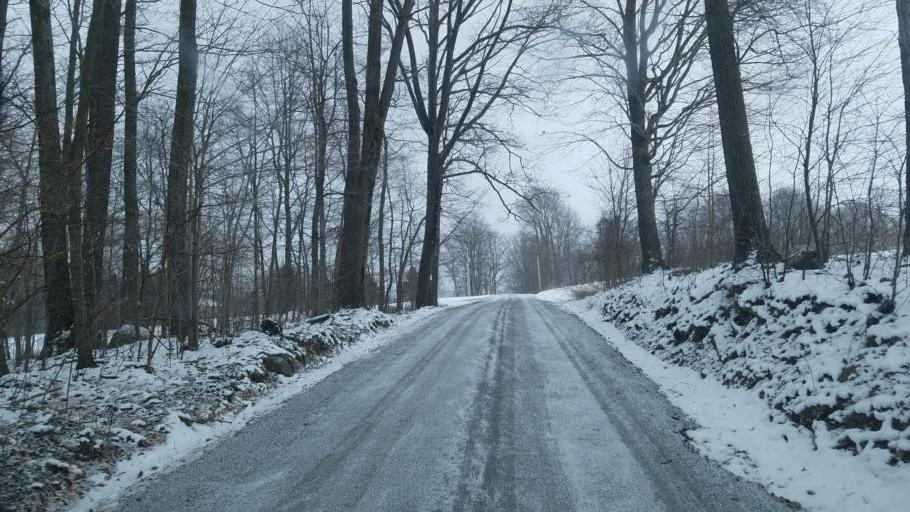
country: US
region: Pennsylvania
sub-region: Venango County
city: Sugarcreek
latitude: 41.4370
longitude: -79.9772
